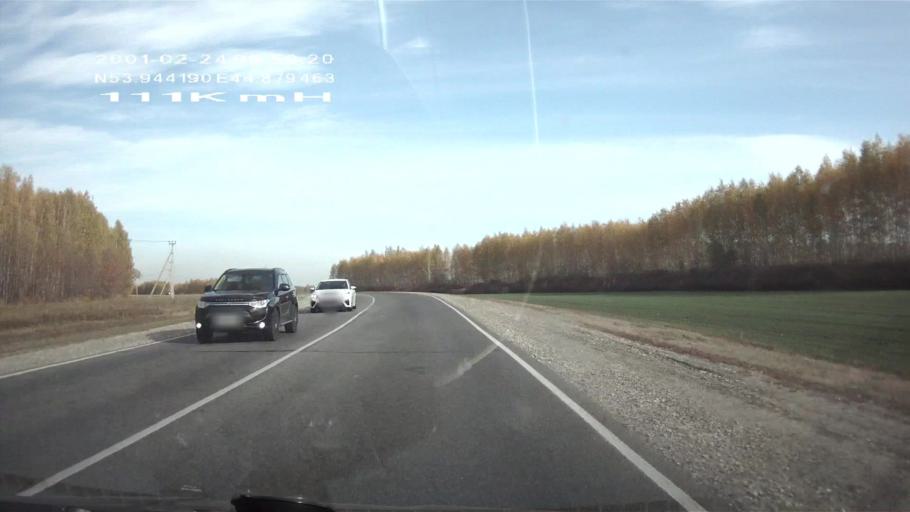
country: RU
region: Penza
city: Issa
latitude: 53.9447
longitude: 44.8798
